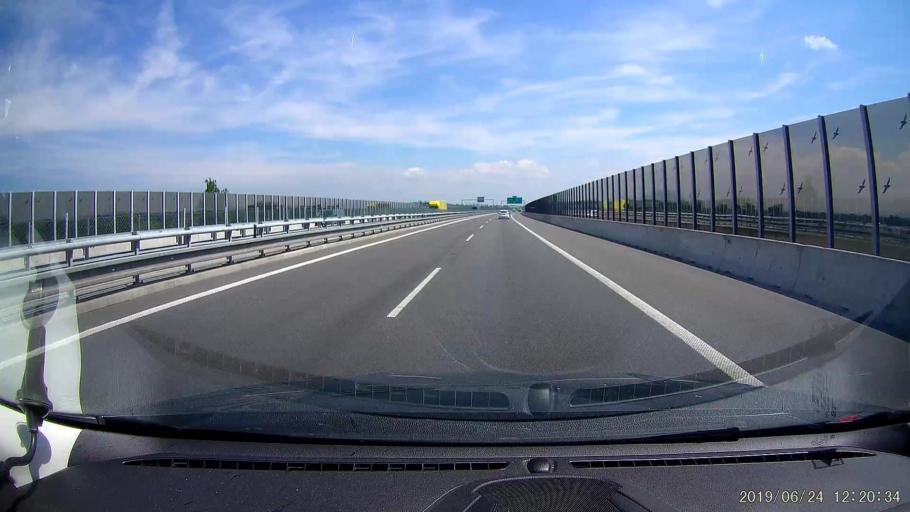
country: CZ
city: Fulnek
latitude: 49.6848
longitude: 17.9446
